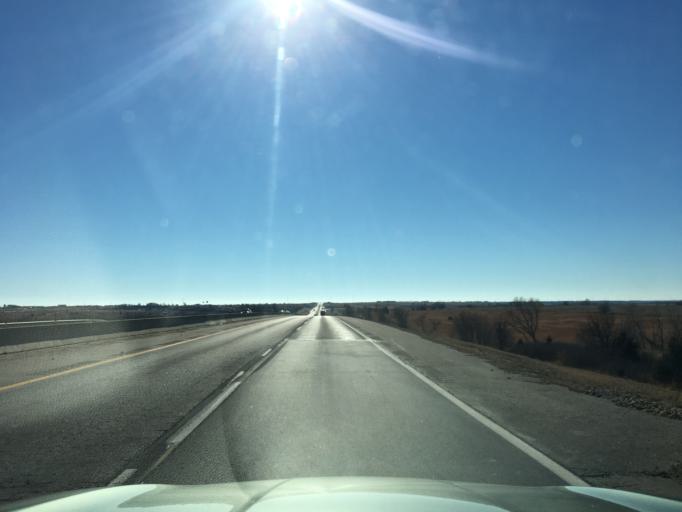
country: US
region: Kansas
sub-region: Sumner County
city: Wellington
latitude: 37.0730
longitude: -97.3386
